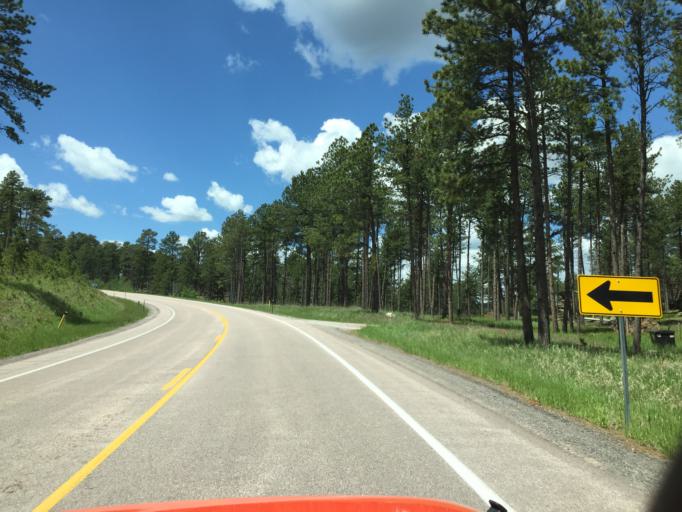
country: US
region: South Dakota
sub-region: Custer County
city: Custer
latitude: 43.9001
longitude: -103.5017
